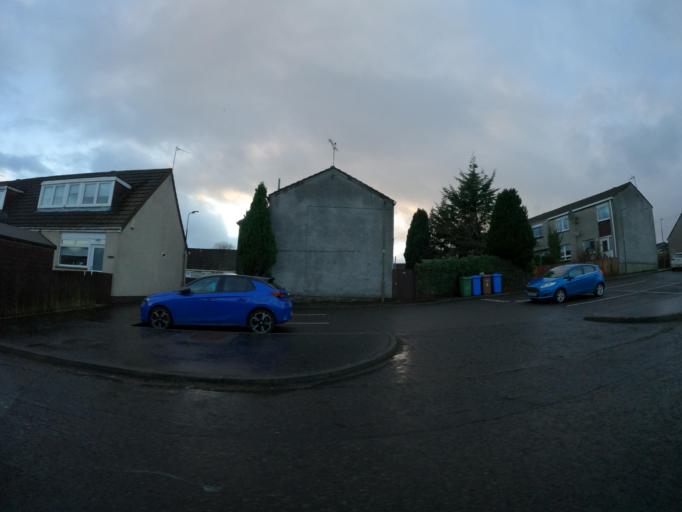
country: GB
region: Scotland
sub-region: West Lothian
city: Livingston
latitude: 55.9261
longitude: -3.5068
